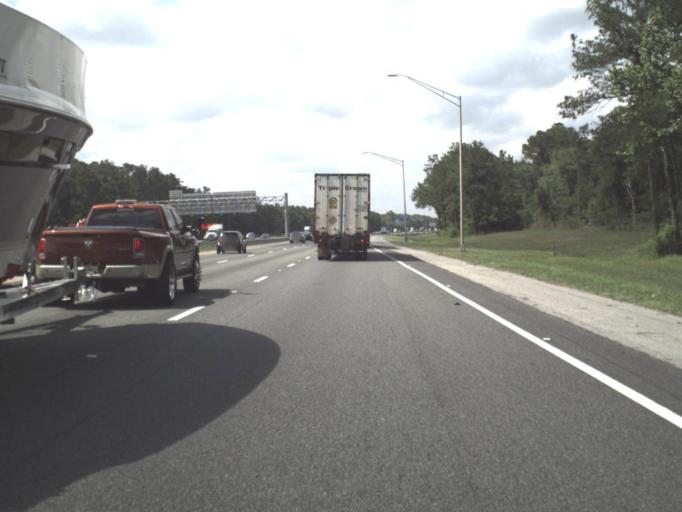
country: US
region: Florida
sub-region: Saint Johns County
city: Fruit Cove
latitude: 30.0705
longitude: -81.4984
